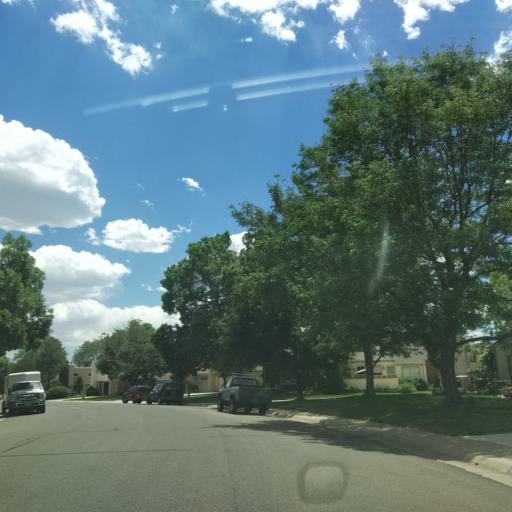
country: US
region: Colorado
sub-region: Jefferson County
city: Lakewood
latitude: 39.6846
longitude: -105.1132
